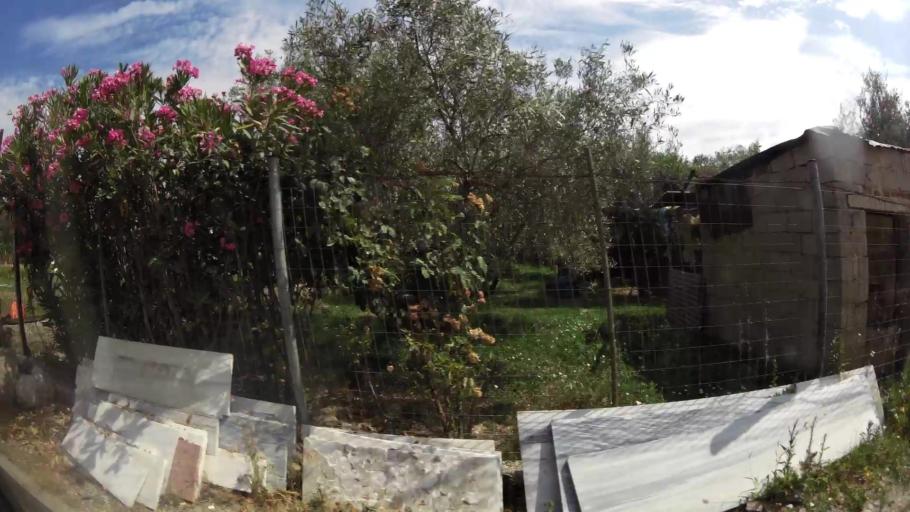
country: GR
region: Central Macedonia
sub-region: Nomos Pierias
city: Katerini
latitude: 40.2667
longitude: 22.4915
